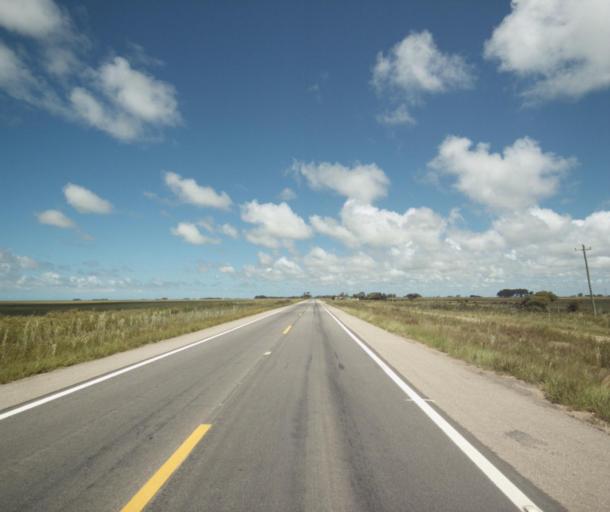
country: UY
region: Cerro Largo
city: Rio Branco
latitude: -32.8612
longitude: -52.7080
